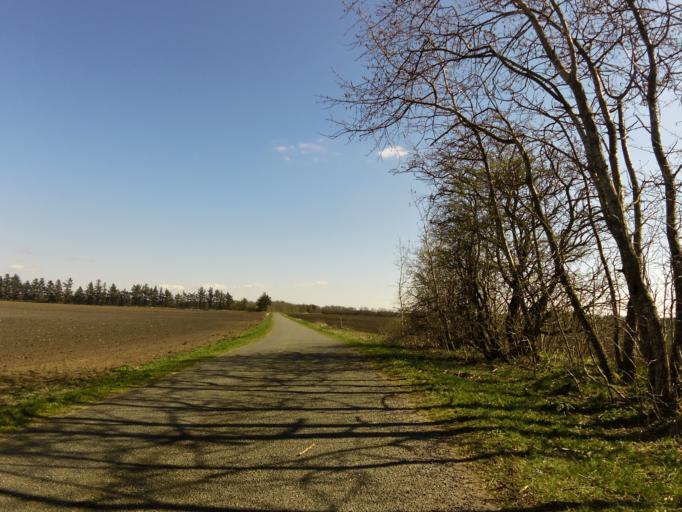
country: DK
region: South Denmark
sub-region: Esbjerg Kommune
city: Ribe
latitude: 55.3381
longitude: 8.8708
